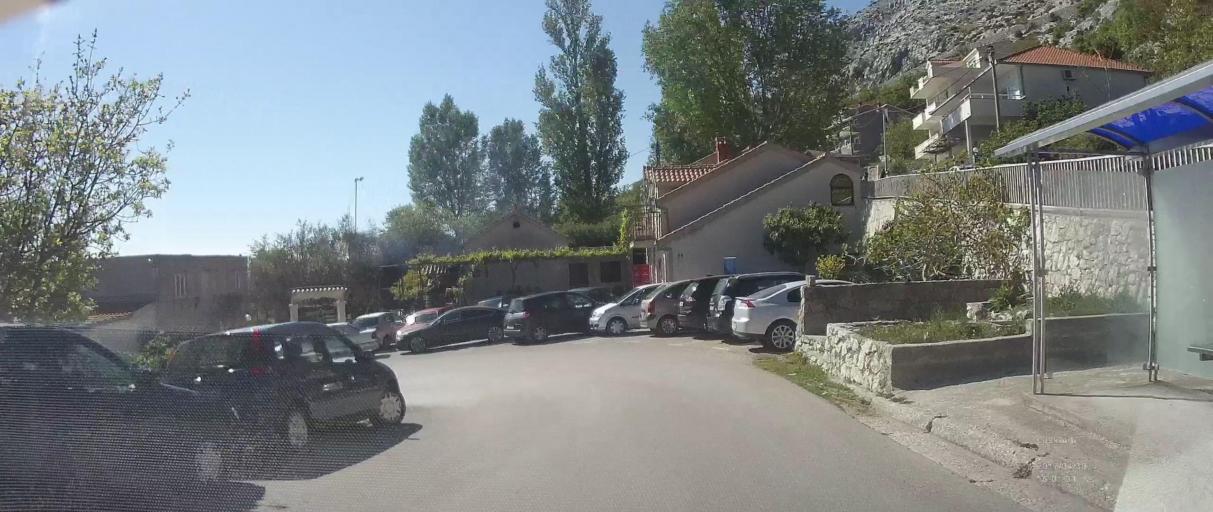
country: HR
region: Splitsko-Dalmatinska
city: Srinjine
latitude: 43.5175
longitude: 16.6091
